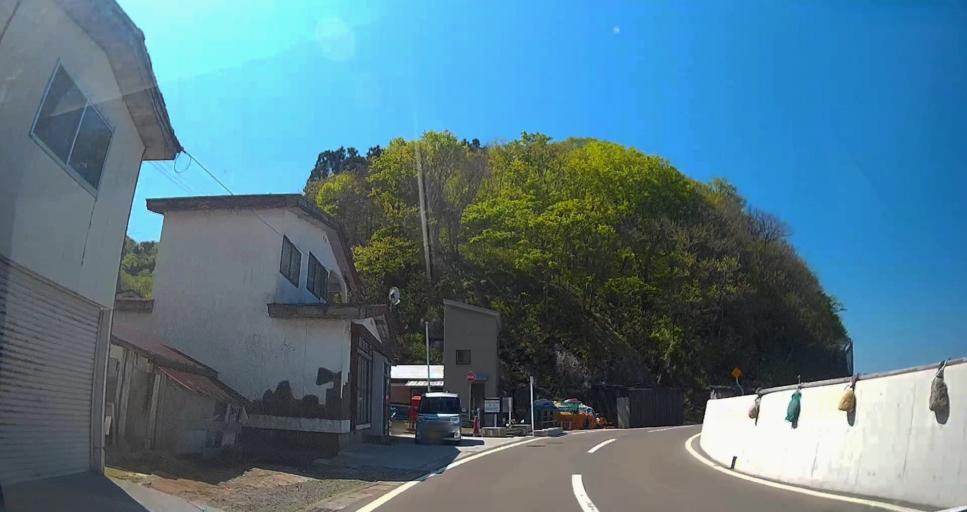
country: JP
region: Aomori
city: Aomori Shi
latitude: 41.1378
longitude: 140.7794
